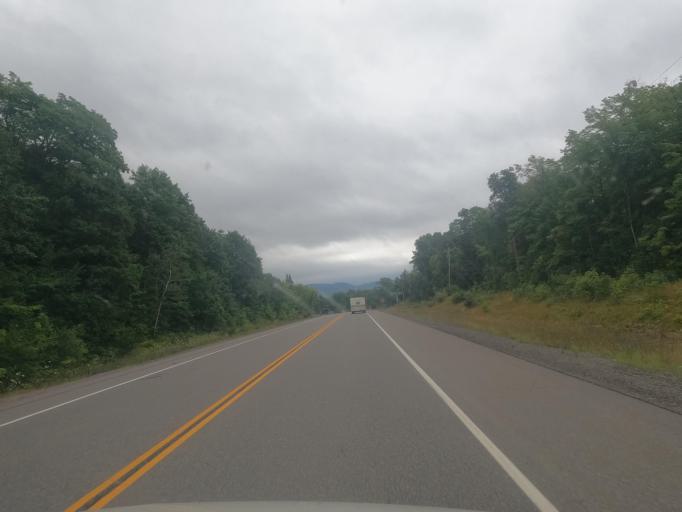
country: CA
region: Ontario
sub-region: Algoma
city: Sault Ste. Marie
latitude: 46.9017
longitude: -84.3806
